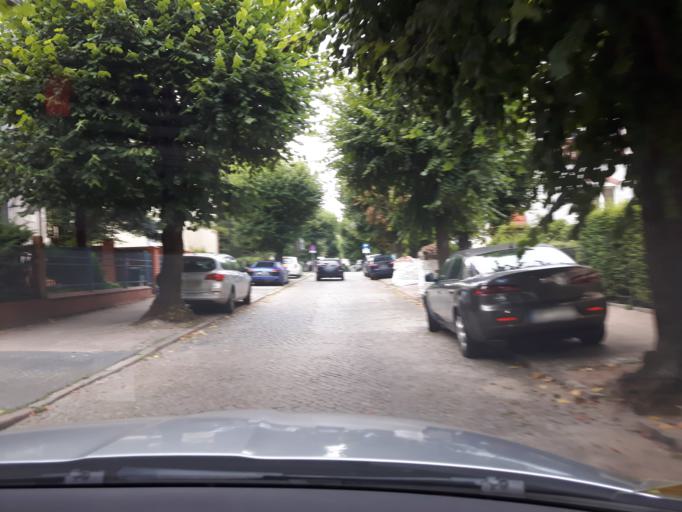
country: PL
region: Pomeranian Voivodeship
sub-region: Sopot
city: Sopot
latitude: 54.4372
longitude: 18.5674
